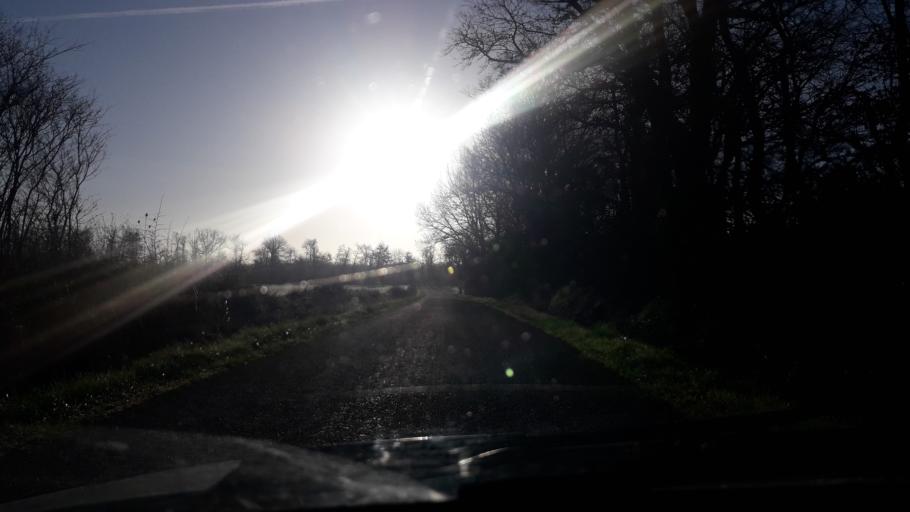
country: FR
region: Midi-Pyrenees
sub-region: Departement du Gers
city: Gimont
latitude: 43.6547
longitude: 0.9799
